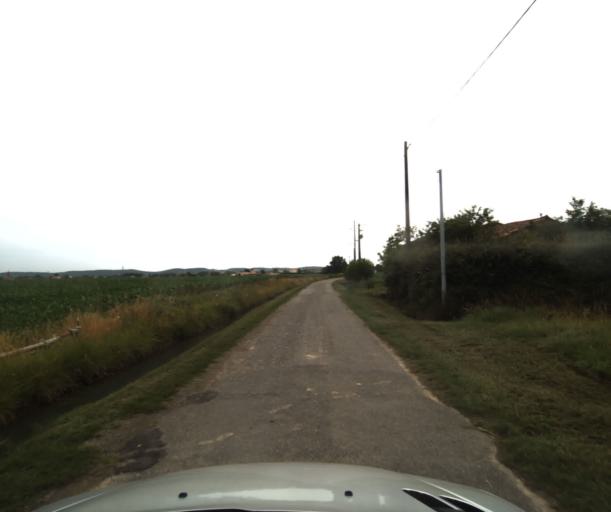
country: FR
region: Midi-Pyrenees
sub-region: Departement de la Haute-Garonne
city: Lacasse
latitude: 43.4199
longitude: 1.2631
